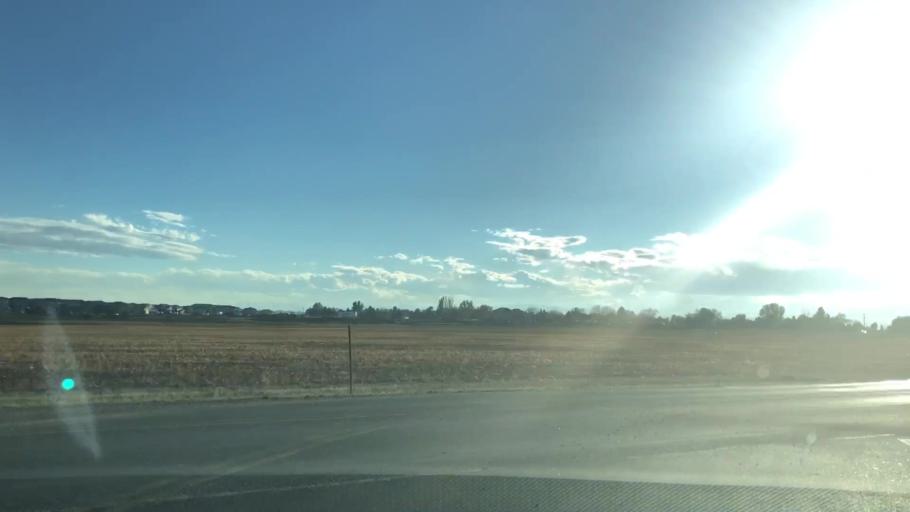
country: US
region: Colorado
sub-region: Larimer County
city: Loveland
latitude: 40.4289
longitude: -105.0150
